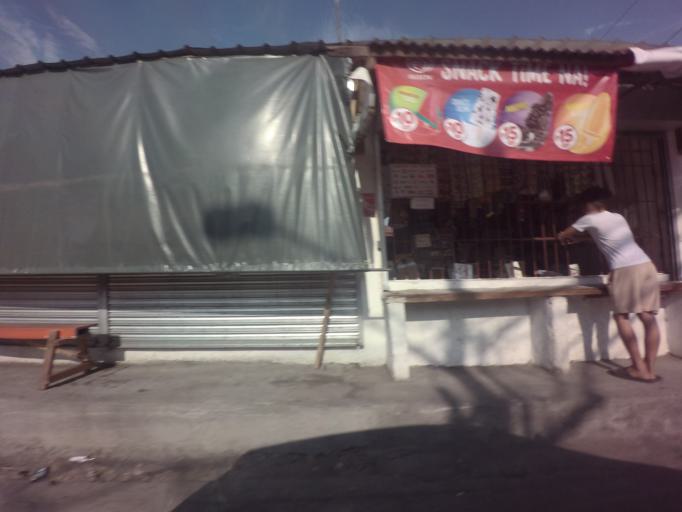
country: PH
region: Calabarzon
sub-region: Province of Rizal
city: Taguig
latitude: 14.4983
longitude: 121.0591
